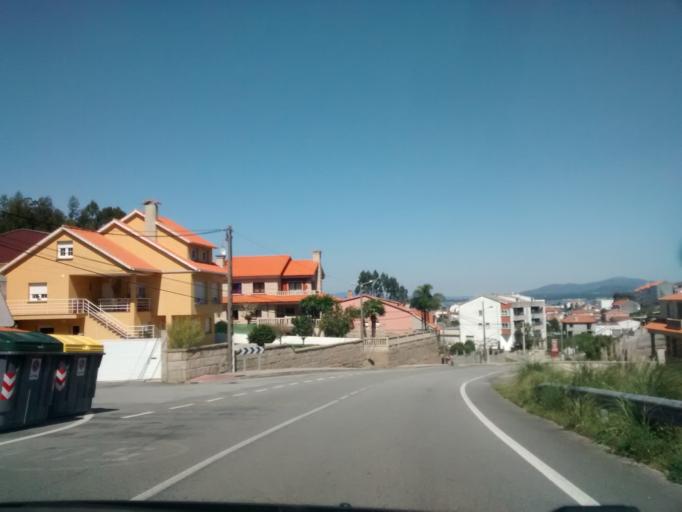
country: ES
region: Galicia
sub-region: Provincia de Pontevedra
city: O Grove
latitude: 42.4850
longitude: -8.8730
